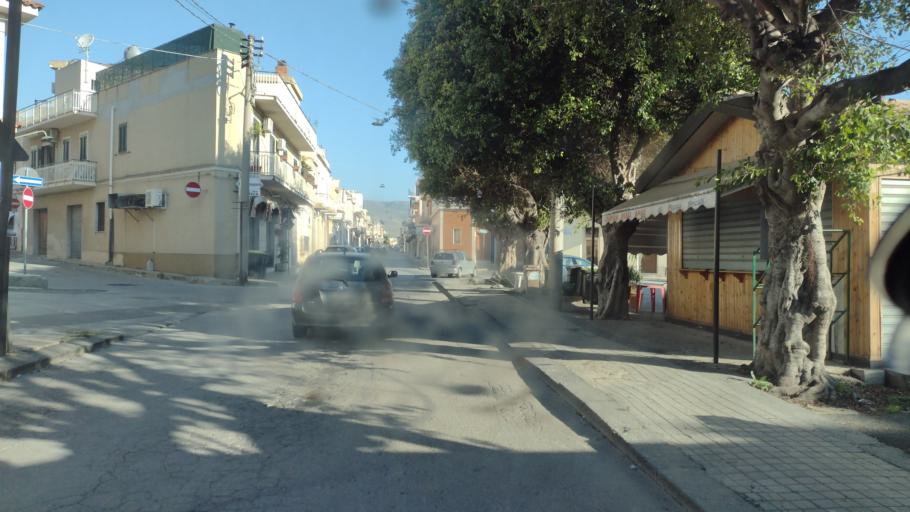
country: IT
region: Sicily
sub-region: Provincia di Siracusa
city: Avola
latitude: 36.9043
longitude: 15.1368
